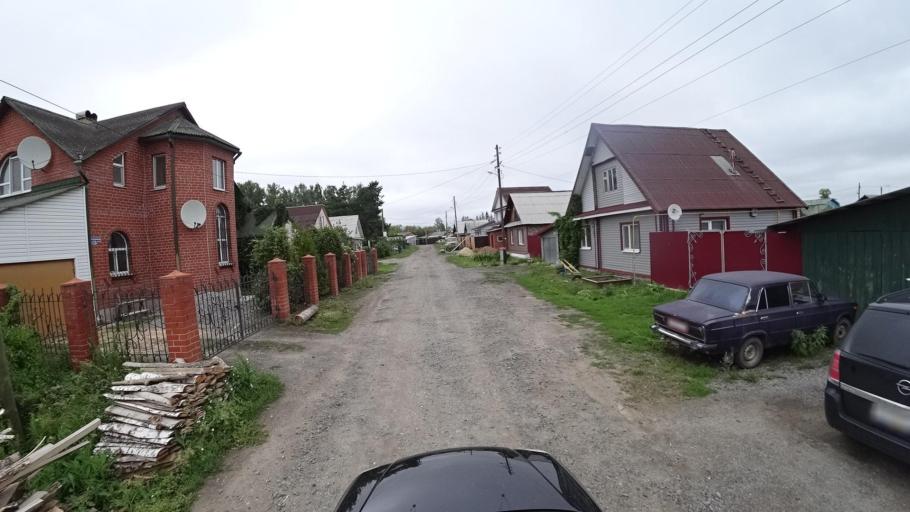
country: RU
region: Sverdlovsk
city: Kamyshlov
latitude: 56.8473
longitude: 62.7605
